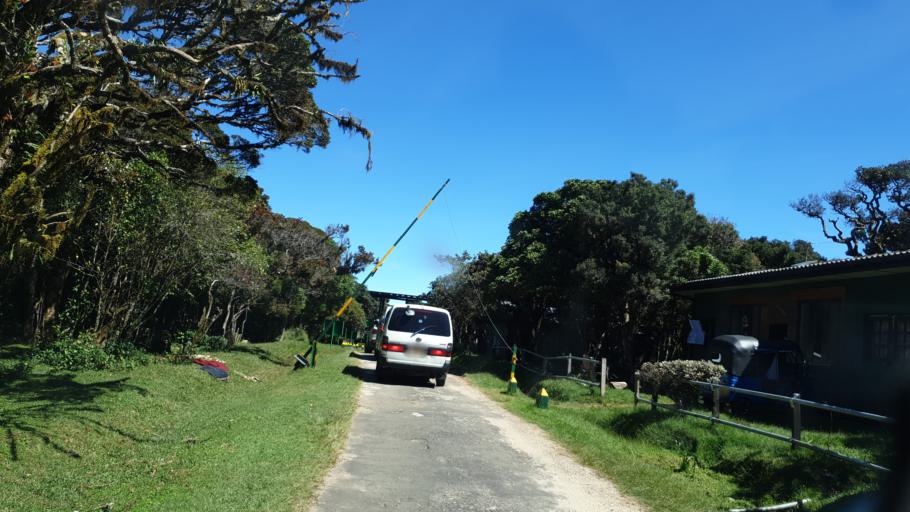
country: LK
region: Uva
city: Haputale
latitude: 6.8068
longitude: 80.8346
